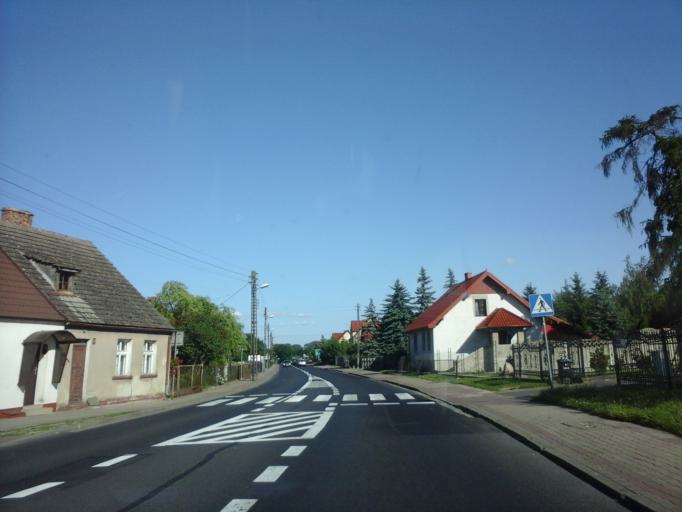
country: PL
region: West Pomeranian Voivodeship
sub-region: Powiat stargardzki
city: Suchan
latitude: 53.2799
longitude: 15.3256
